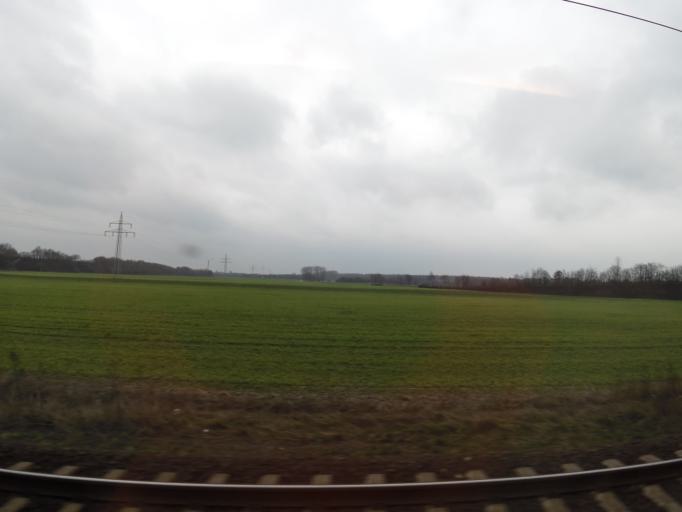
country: DE
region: North Rhine-Westphalia
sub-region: Regierungsbezirk Detmold
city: Minden
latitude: 52.2898
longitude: 8.9771
